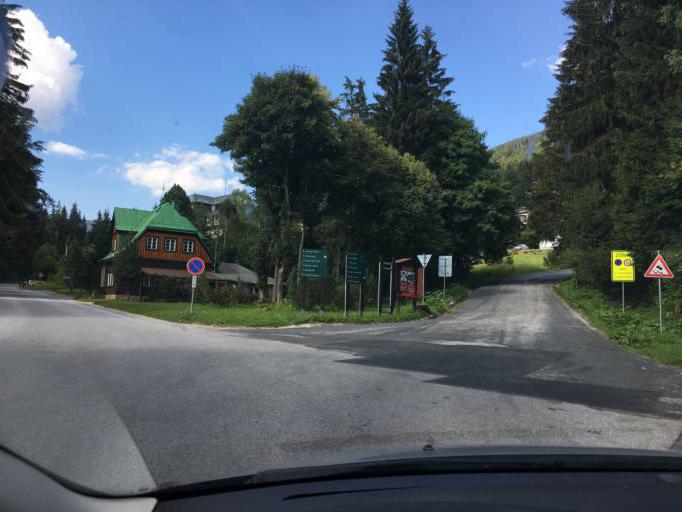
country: CZ
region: Kralovehradecky
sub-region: Okres Trutnov
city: Spindleruv Mlyn
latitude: 50.7292
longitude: 15.6087
